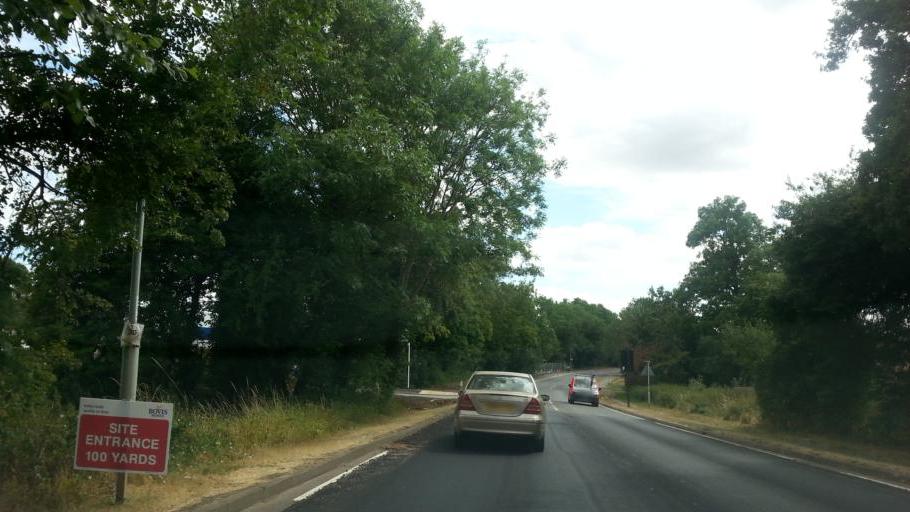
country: GB
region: England
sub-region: Northamptonshire
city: Silverstone
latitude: 52.0907
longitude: -1.0219
